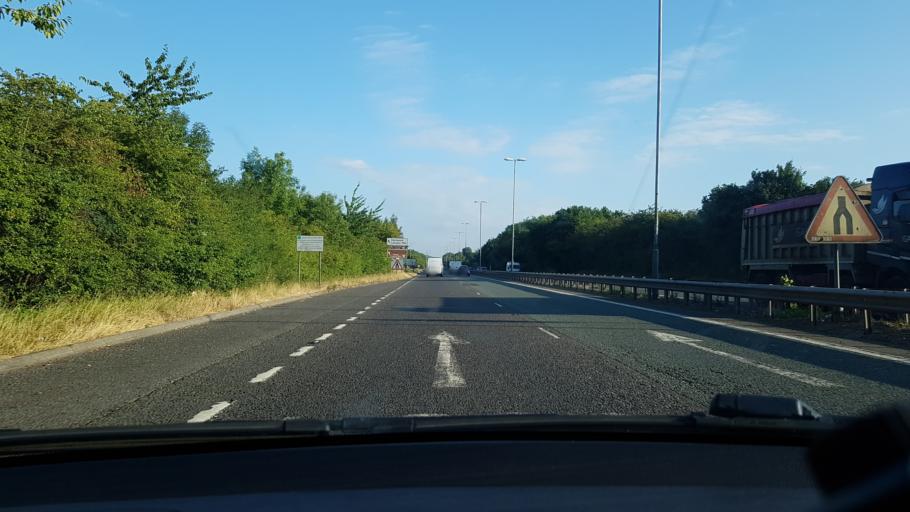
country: GB
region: England
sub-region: Nottinghamshire
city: Eastwood
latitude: 53.0126
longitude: -1.3155
